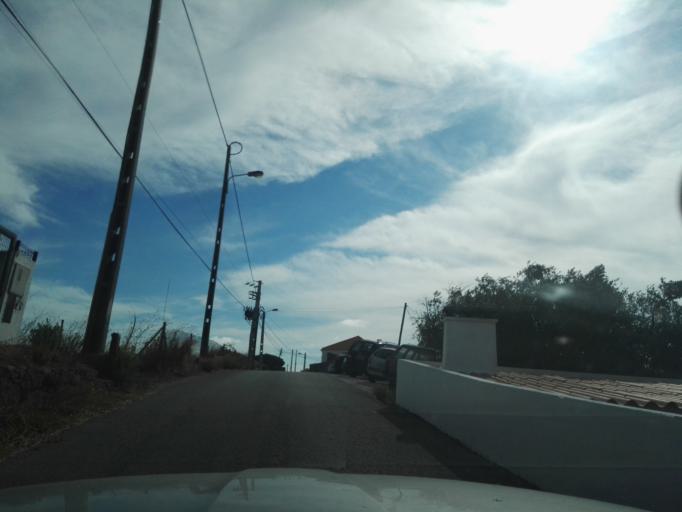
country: PT
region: Lisbon
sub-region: Vila Franca de Xira
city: Sao Joao dos Montes
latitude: 38.9601
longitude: -9.0241
